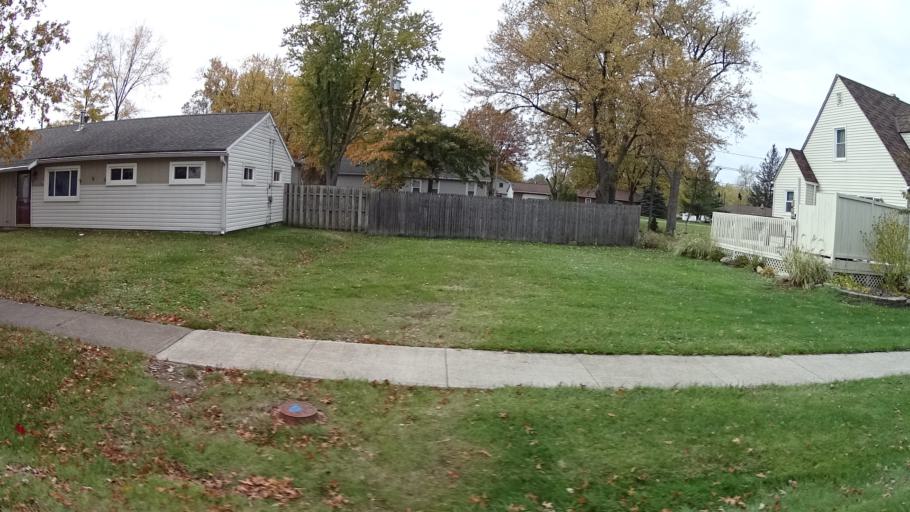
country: US
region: Ohio
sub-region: Lorain County
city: Sheffield Lake
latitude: 41.4864
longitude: -82.1031
